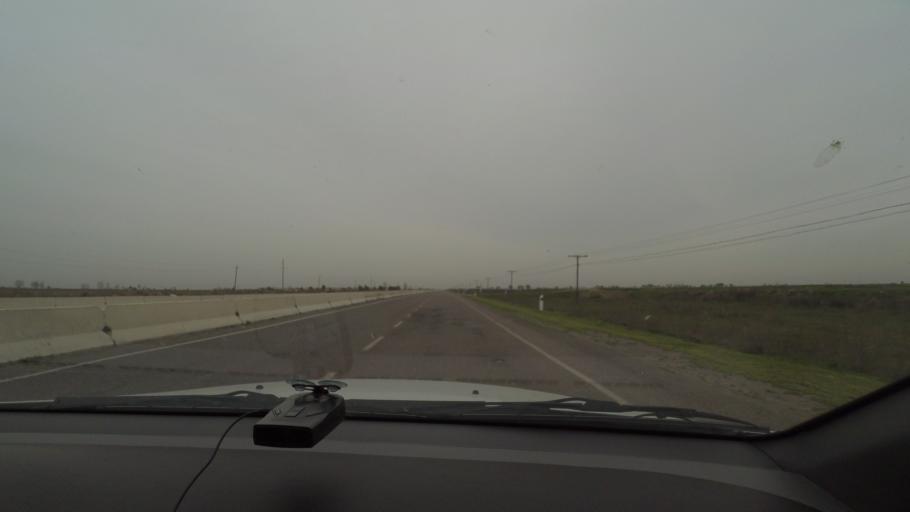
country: UZ
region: Sirdaryo
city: Guliston
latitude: 40.4939
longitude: 68.6617
